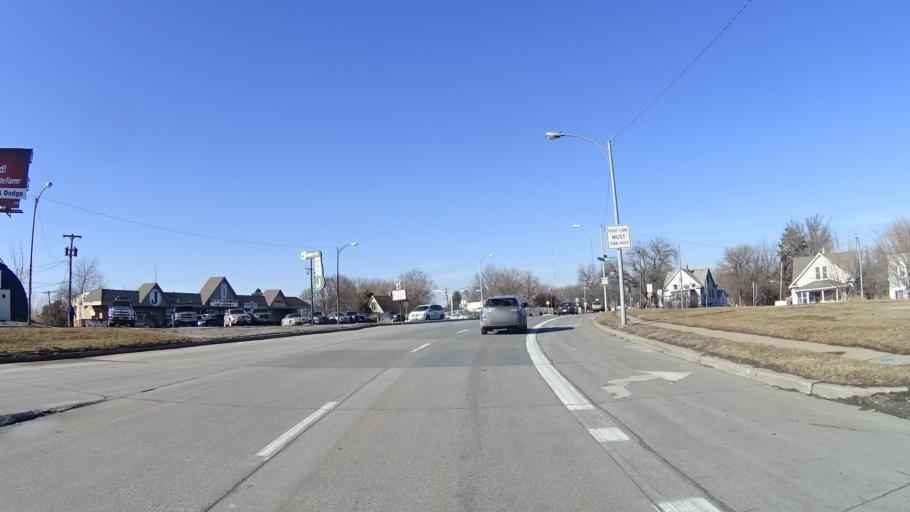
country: US
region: Nebraska
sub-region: Douglas County
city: Omaha
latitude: 41.2872
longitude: -96.0093
